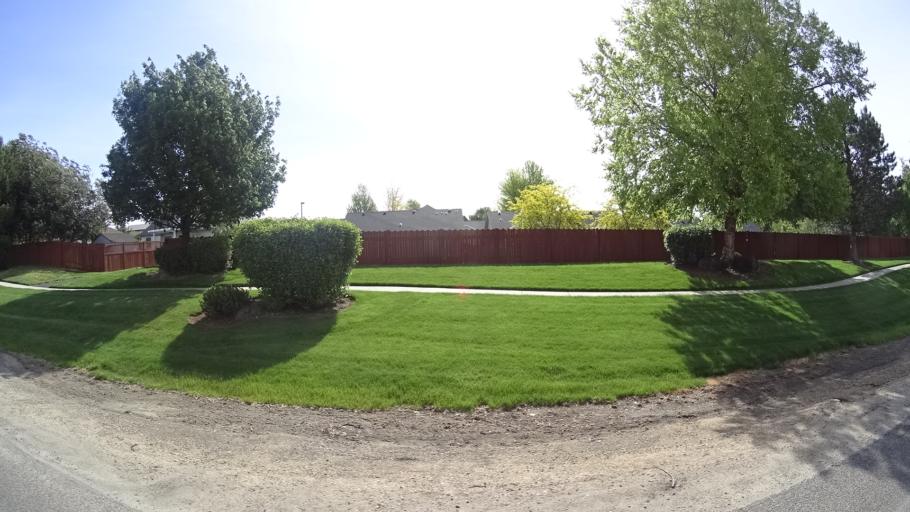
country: US
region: Idaho
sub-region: Ada County
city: Meridian
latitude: 43.5599
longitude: -116.3344
